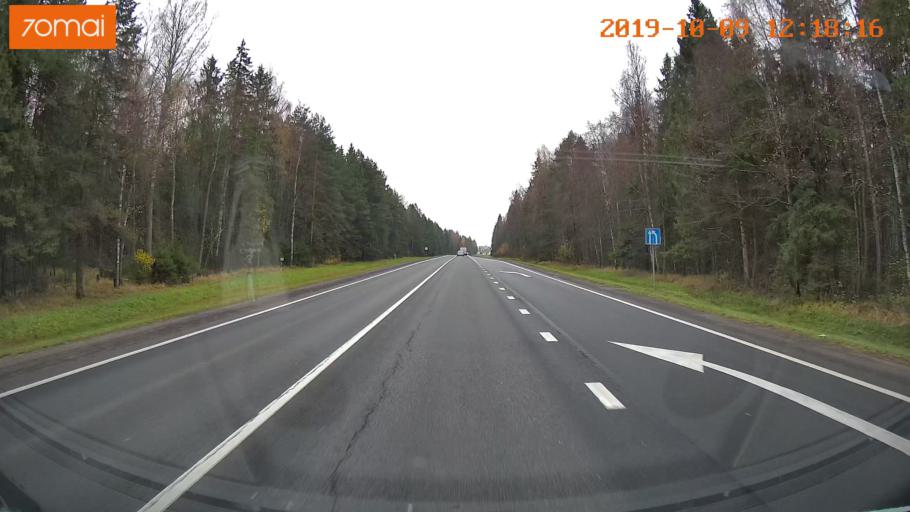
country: RU
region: Jaroslavl
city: Prechistoye
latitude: 58.4447
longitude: 40.3211
